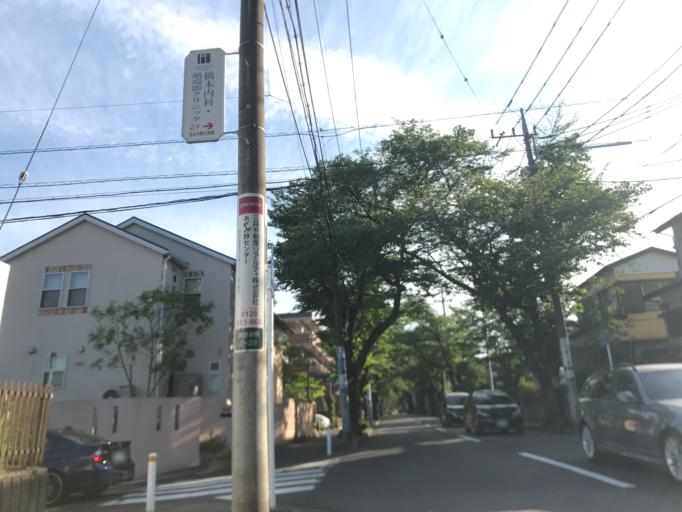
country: JP
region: Tokyo
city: Chofugaoka
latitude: 35.5685
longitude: 139.5455
